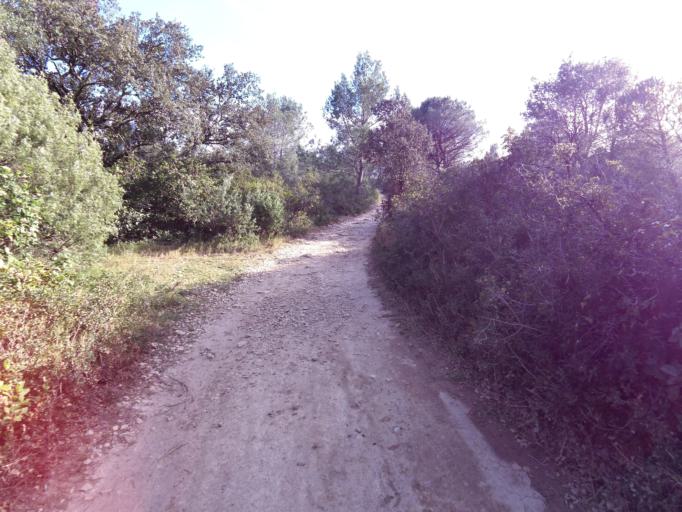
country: FR
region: Languedoc-Roussillon
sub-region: Departement du Gard
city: Congenies
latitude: 43.7837
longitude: 4.1752
